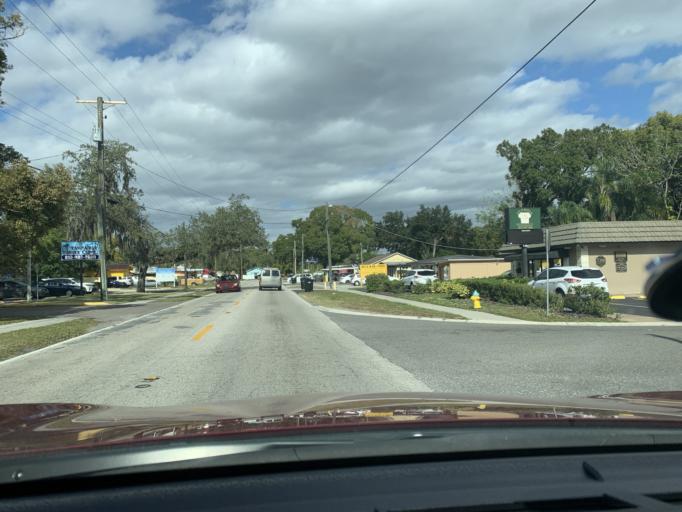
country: US
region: Florida
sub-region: Hillsborough County
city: Egypt Lake-Leto
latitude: 28.0142
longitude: -82.4852
